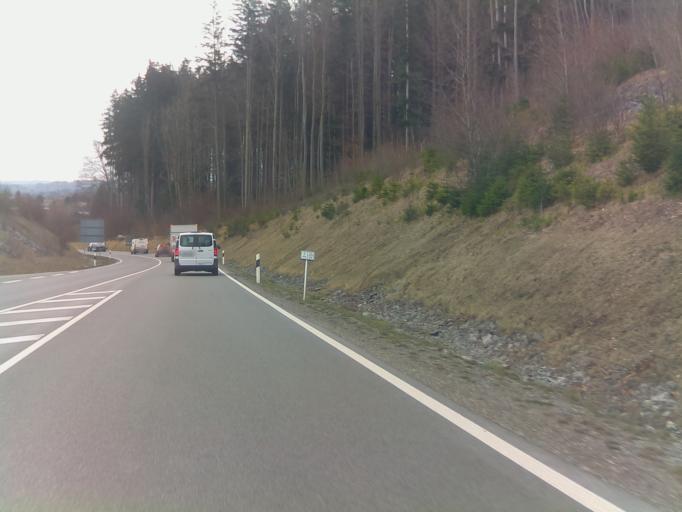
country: DE
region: Bavaria
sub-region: Upper Bavaria
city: Peissenberg
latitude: 47.7809
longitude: 11.0421
